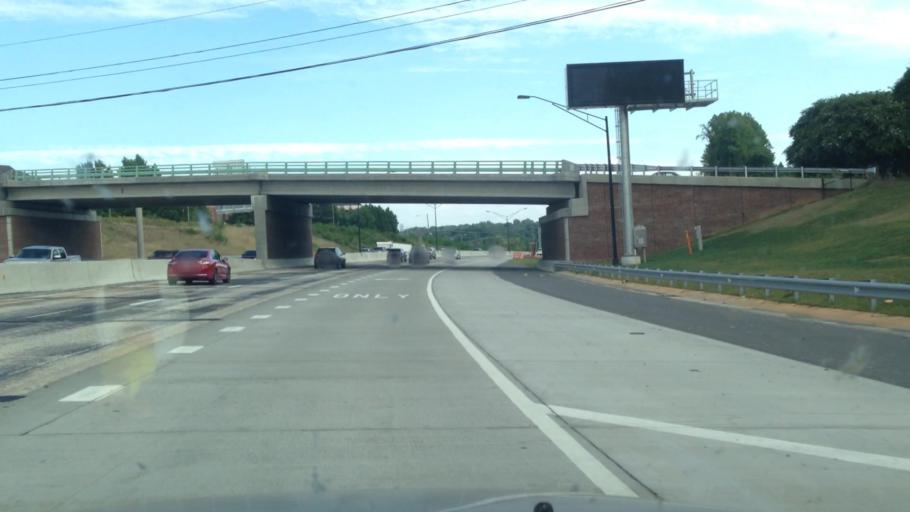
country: US
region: North Carolina
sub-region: Forsyth County
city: Winston-Salem
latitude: 36.0911
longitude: -80.2300
